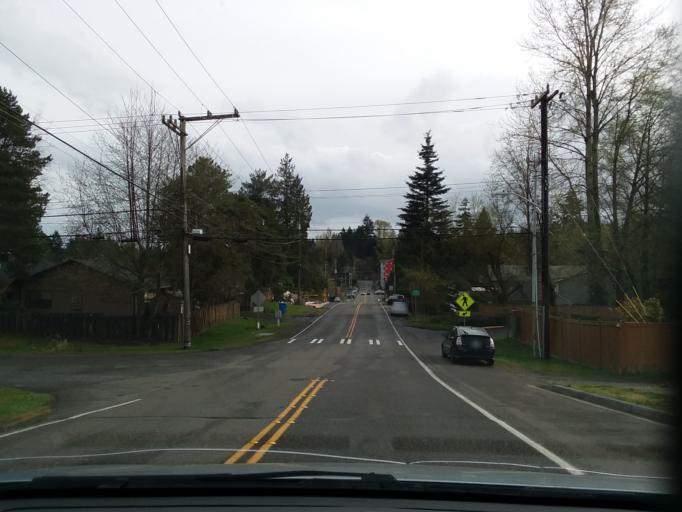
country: US
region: Washington
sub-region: Snohomish County
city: Mountlake Terrace
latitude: 47.7739
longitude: -122.3030
